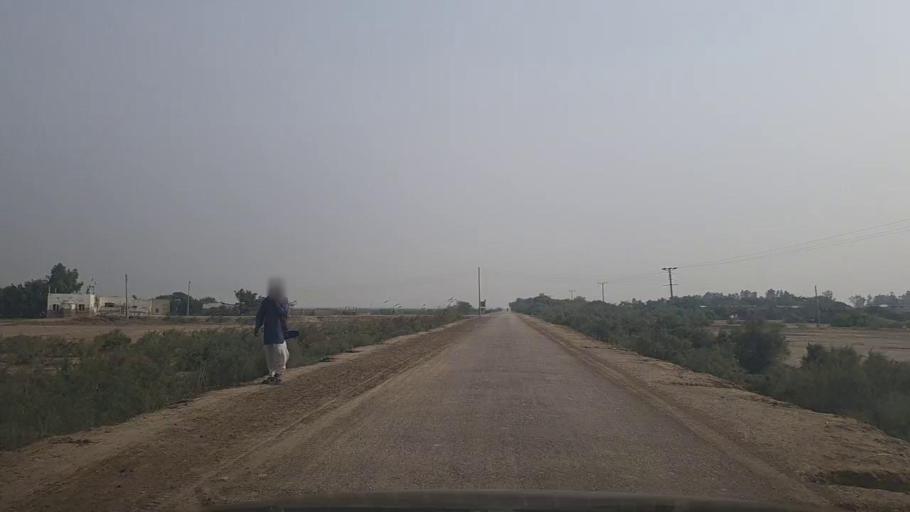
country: PK
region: Sindh
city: Mirpur Sakro
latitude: 24.4713
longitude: 67.6736
